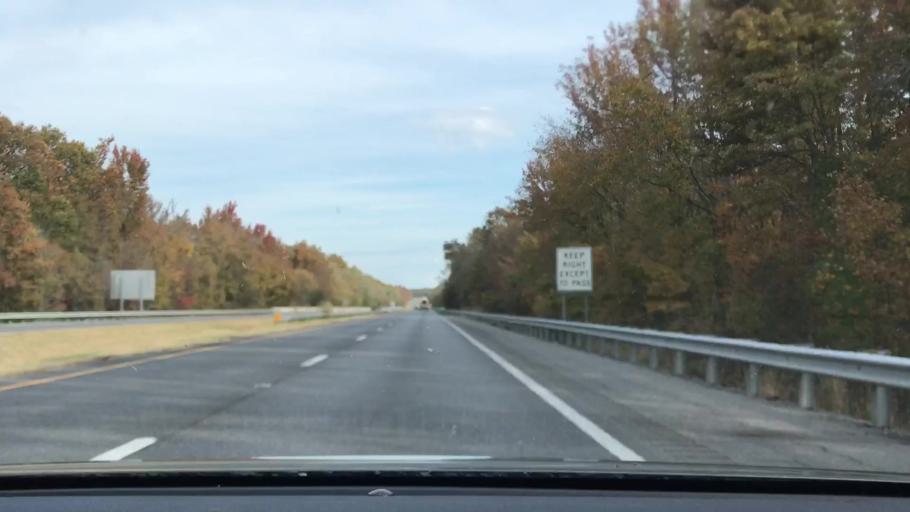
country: US
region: Kentucky
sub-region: Marshall County
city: Benton
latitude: 36.8771
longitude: -88.3600
